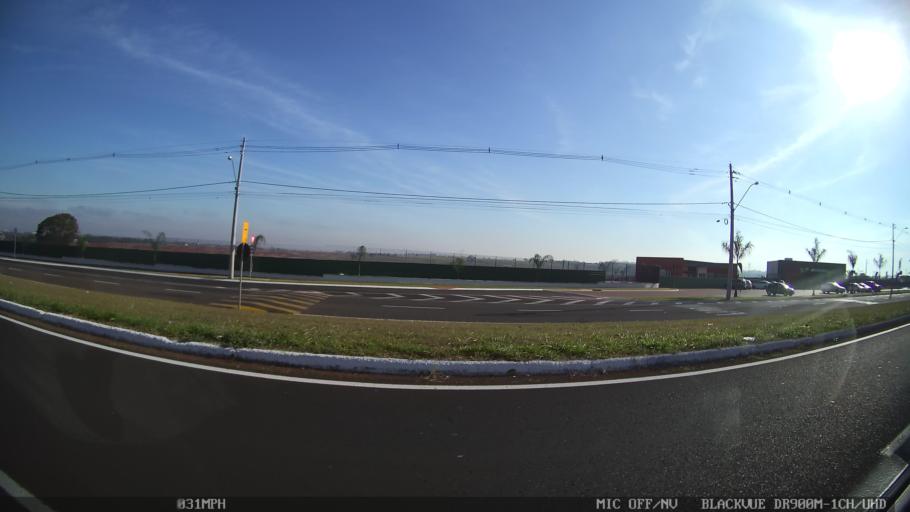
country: BR
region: Sao Paulo
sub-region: Sao Jose Do Rio Preto
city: Sao Jose do Rio Preto
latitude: -20.7744
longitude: -49.3346
